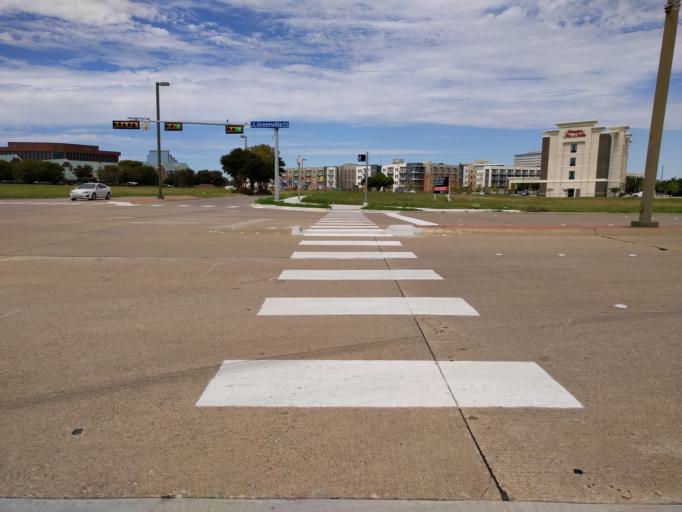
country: US
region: Texas
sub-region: Dallas County
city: Richardson
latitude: 32.9796
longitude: -96.7059
